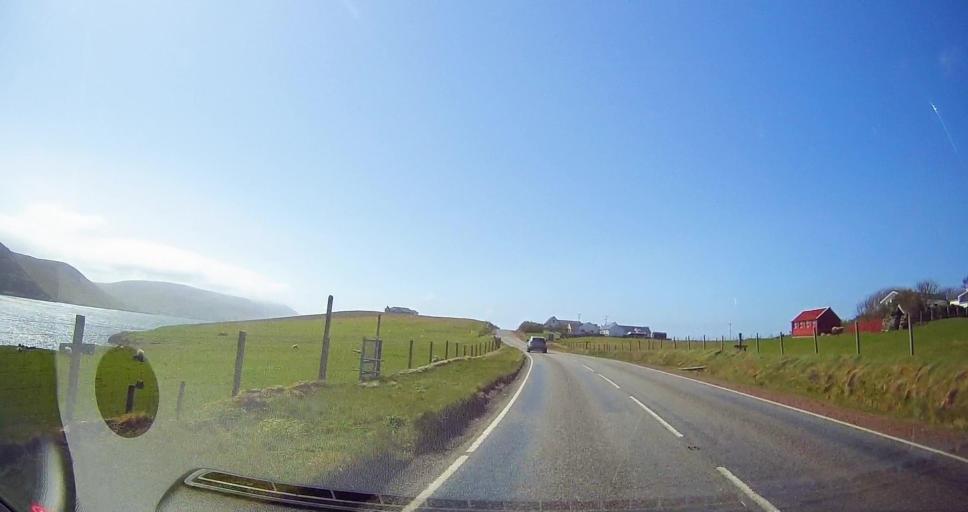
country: GB
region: Scotland
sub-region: Shetland Islands
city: Sandwick
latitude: 60.1250
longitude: -1.2842
